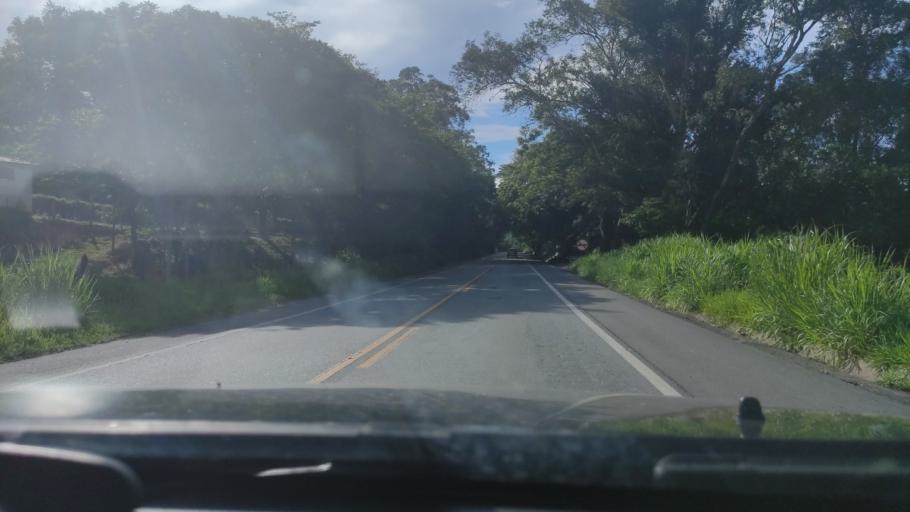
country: BR
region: Sao Paulo
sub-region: Aguas De Lindoia
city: Aguas de Lindoia
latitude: -22.5098
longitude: -46.6707
